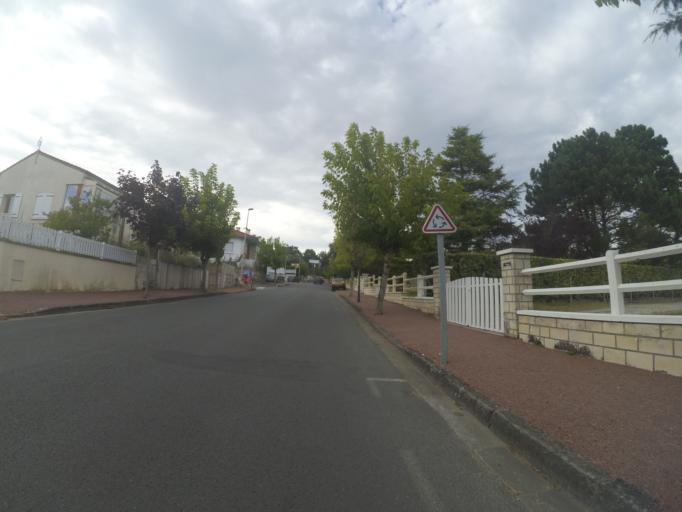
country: FR
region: Poitou-Charentes
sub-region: Departement de la Charente-Maritime
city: Meschers-sur-Gironde
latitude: 45.5643
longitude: -0.9605
